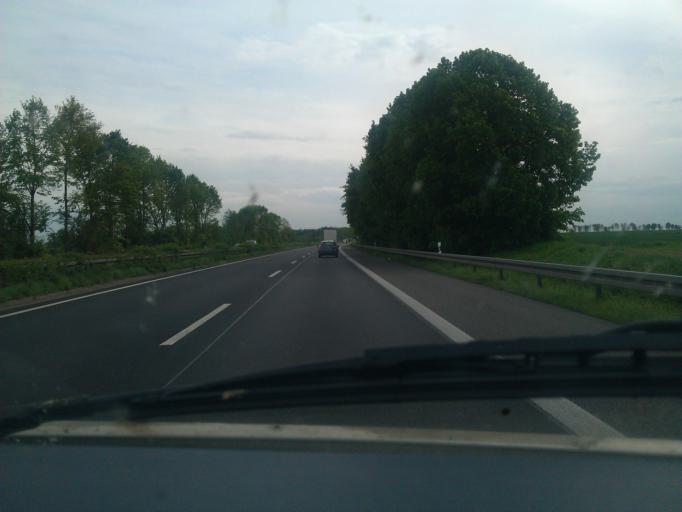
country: DE
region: North Rhine-Westphalia
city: Julich
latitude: 50.9768
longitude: 6.3747
